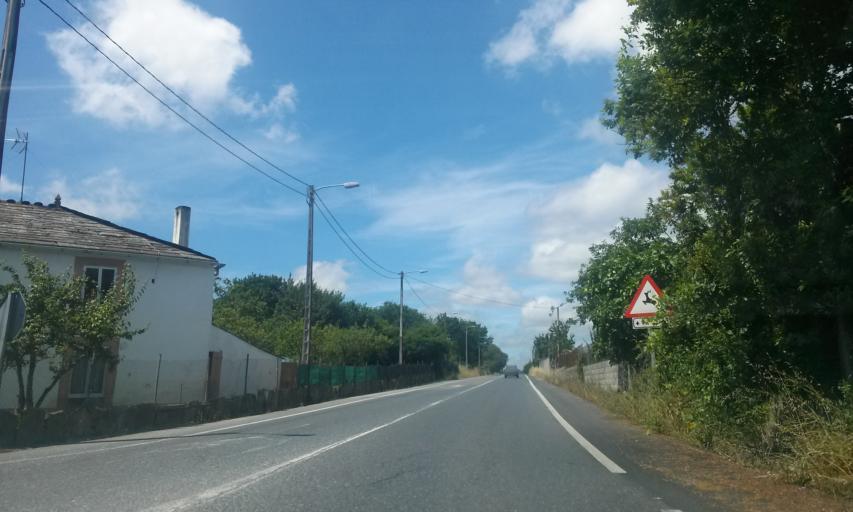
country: ES
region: Galicia
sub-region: Provincia de Lugo
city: Lugo
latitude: 42.9887
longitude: -7.5794
